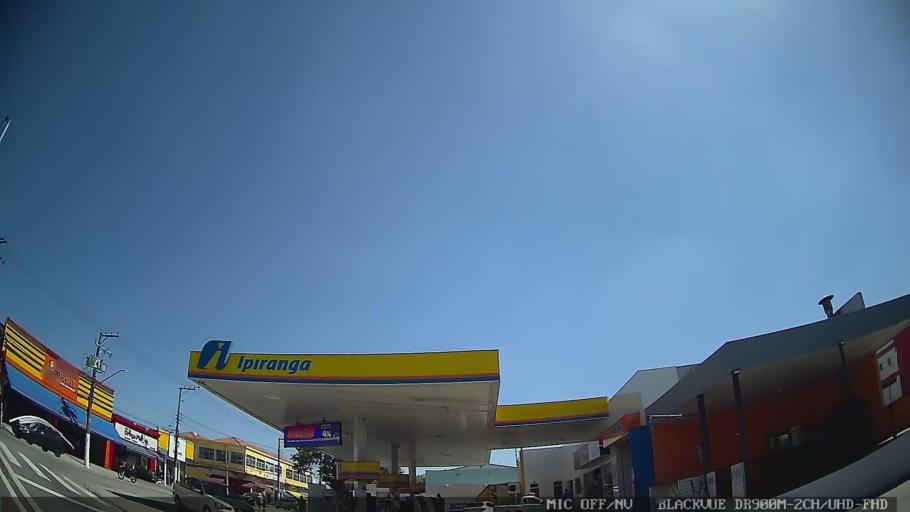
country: BR
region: Sao Paulo
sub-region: Sao Caetano Do Sul
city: Sao Caetano do Sul
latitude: -23.5768
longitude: -46.5167
